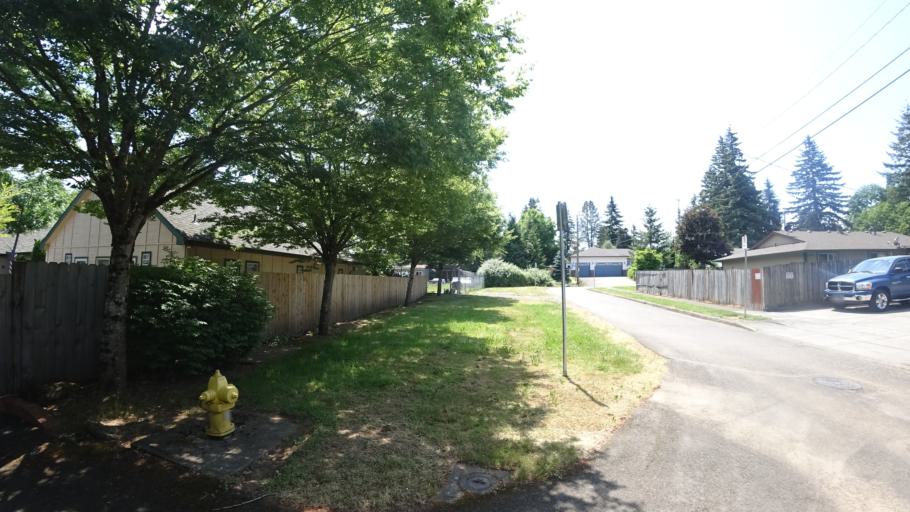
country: US
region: Oregon
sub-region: Multnomah County
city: Fairview
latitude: 45.5290
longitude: -122.4974
